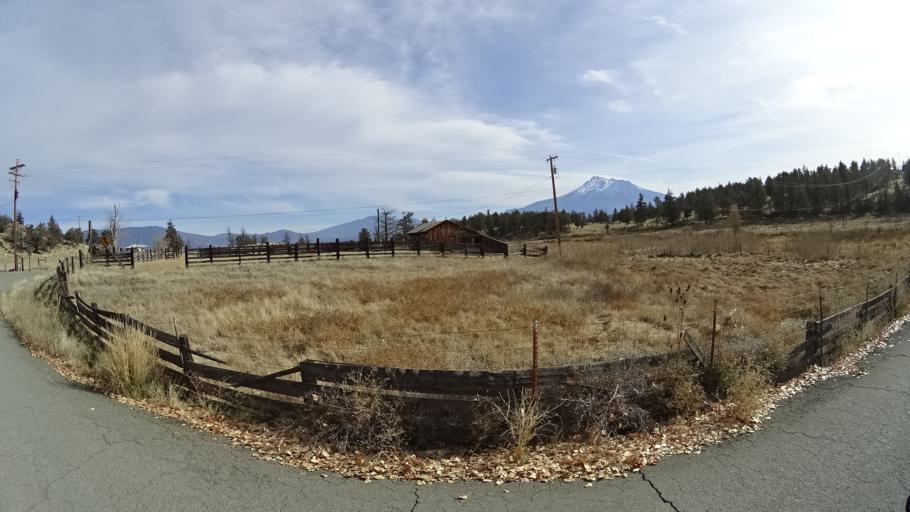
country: US
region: California
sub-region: Siskiyou County
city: Montague
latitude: 41.5914
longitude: -122.4379
